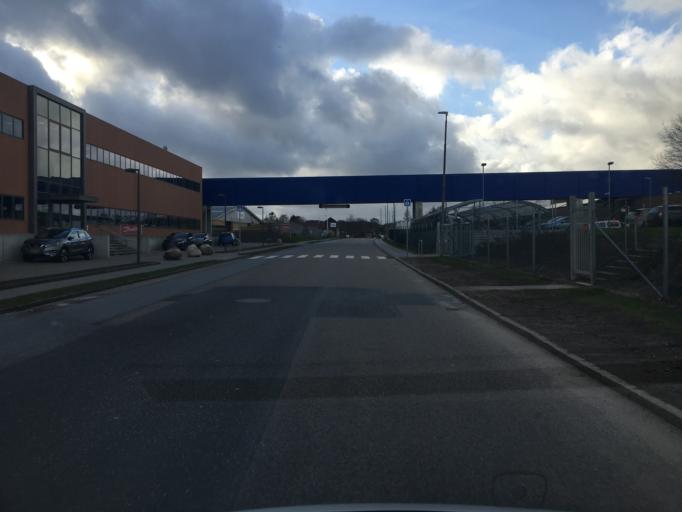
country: DK
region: South Denmark
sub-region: Sonderborg Kommune
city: Grasten
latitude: 54.9124
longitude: 9.5929
